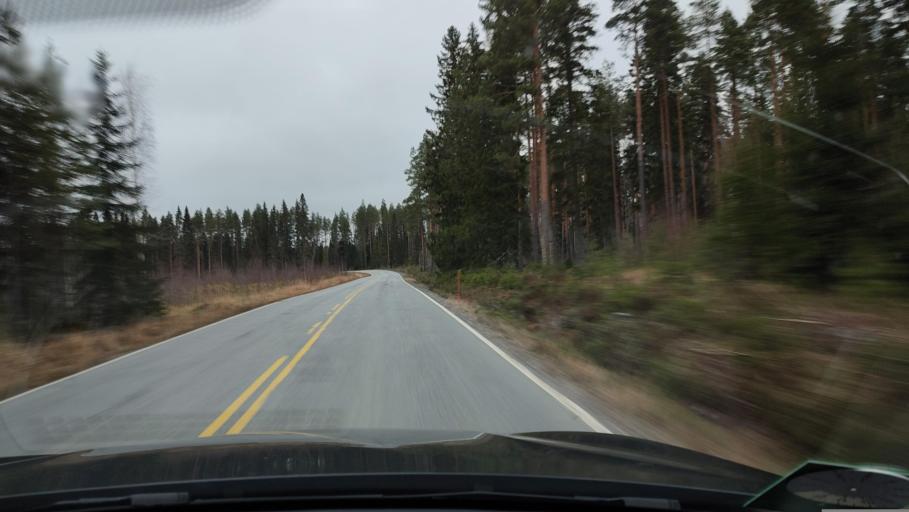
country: FI
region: Southern Ostrobothnia
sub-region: Suupohja
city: Karijoki
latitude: 62.2412
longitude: 21.7587
